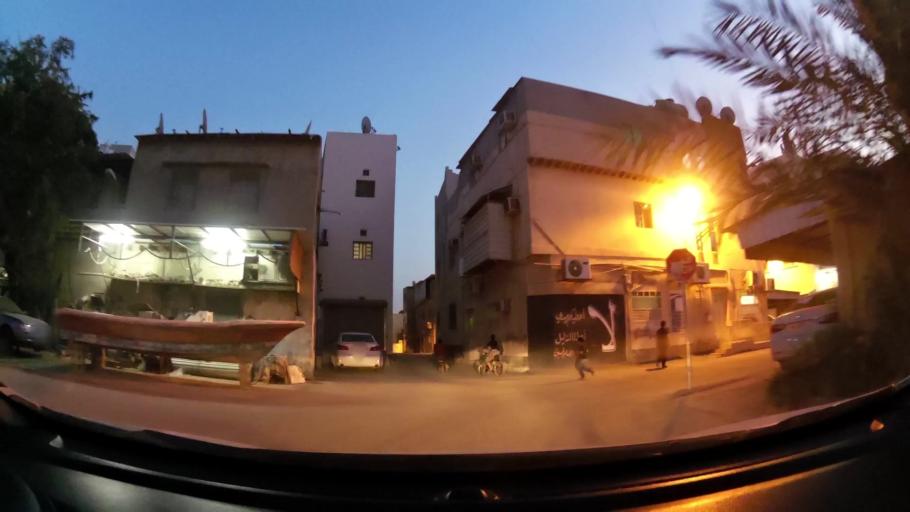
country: BH
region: Manama
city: Jidd Hafs
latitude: 26.2034
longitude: 50.5529
